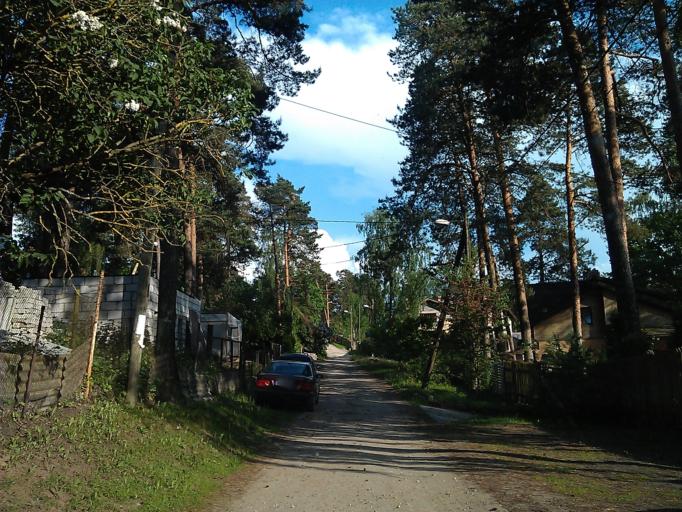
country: LV
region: Riga
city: Bergi
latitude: 56.9826
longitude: 24.3029
